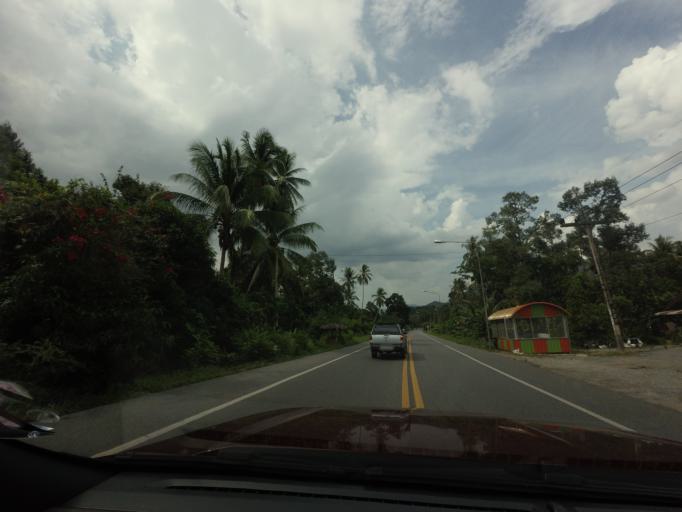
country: TH
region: Yala
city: Ban Nang Sata
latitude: 6.2749
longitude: 101.2848
